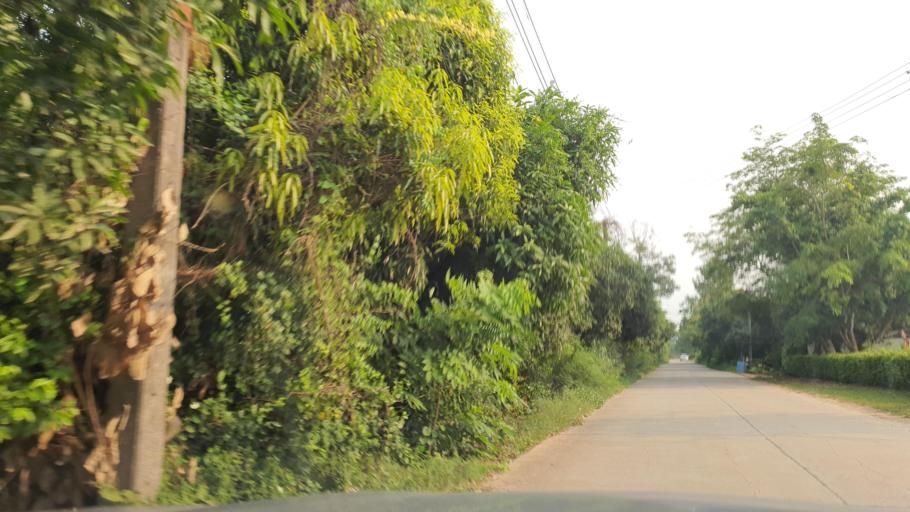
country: TH
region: Rayong
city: Rayong
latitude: 12.6088
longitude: 101.4005
